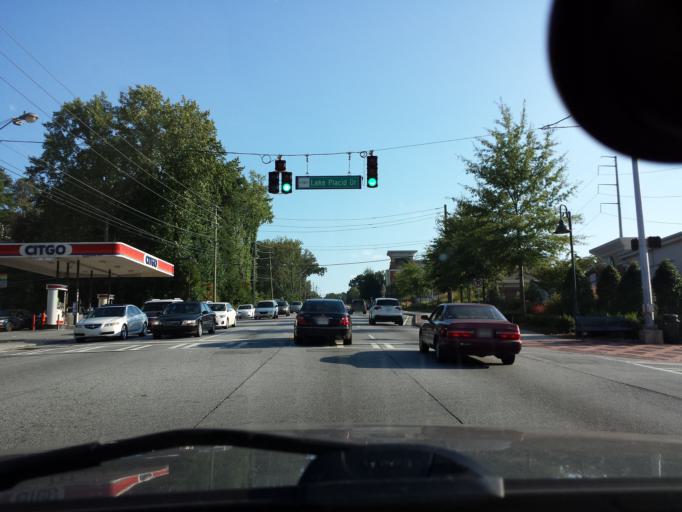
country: US
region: Georgia
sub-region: Fulton County
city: Sandy Springs
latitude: 33.9091
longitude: -84.3788
